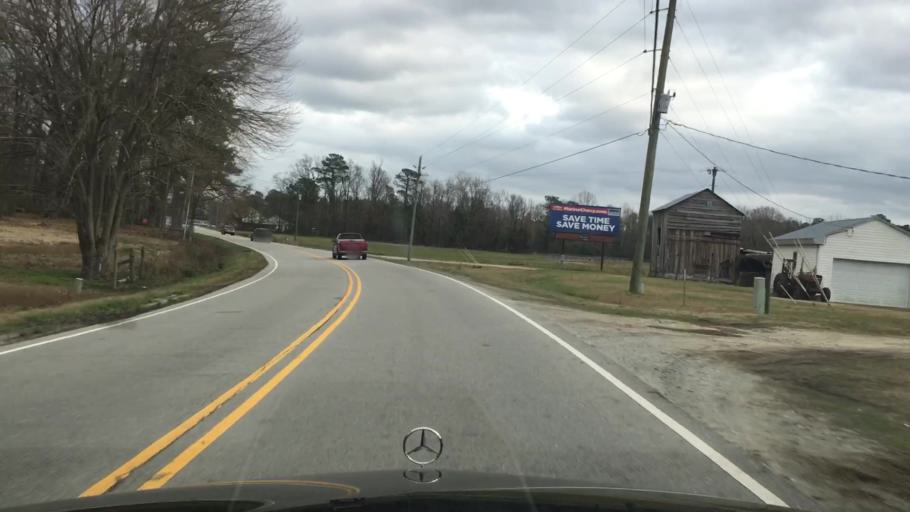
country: US
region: North Carolina
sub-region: Onslow County
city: Richlands
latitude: 34.8784
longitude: -77.5171
